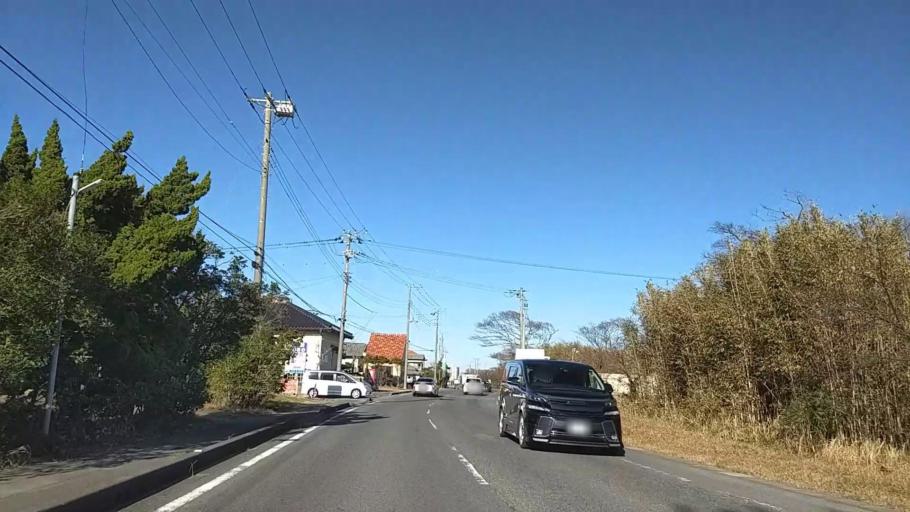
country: JP
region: Chiba
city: Mobara
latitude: 35.4370
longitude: 140.3981
